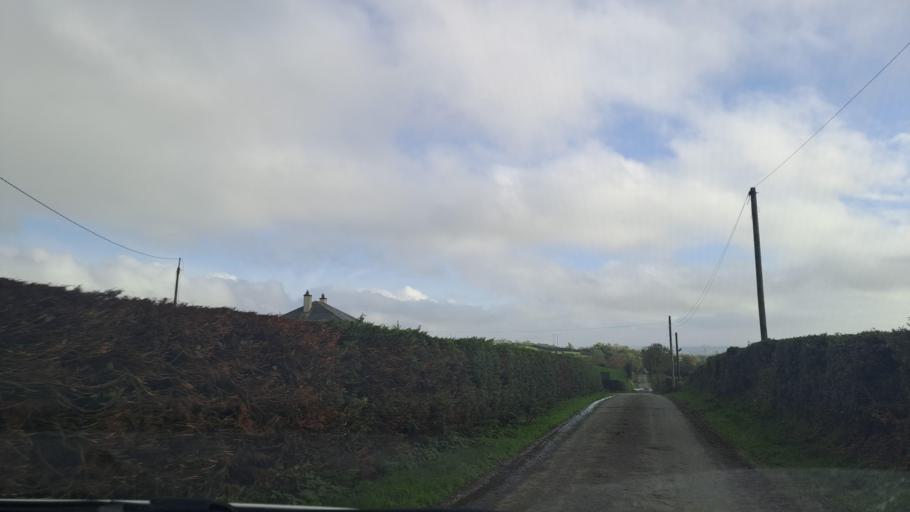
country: IE
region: Ulster
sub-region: County Monaghan
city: Carrickmacross
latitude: 54.0243
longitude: -6.7698
